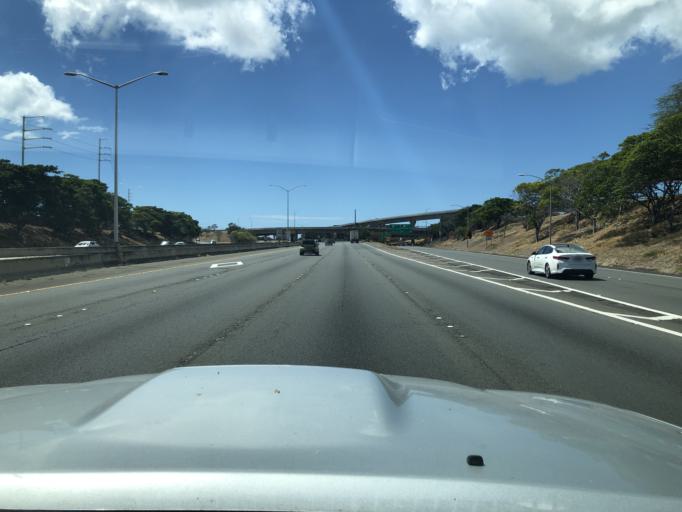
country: US
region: Hawaii
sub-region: Honolulu County
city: Hickam Field
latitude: 21.3504
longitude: -157.9331
